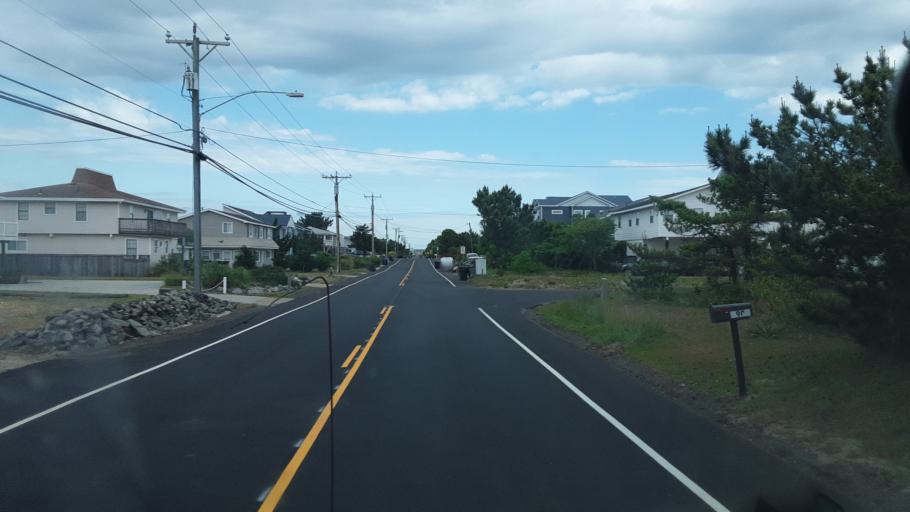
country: US
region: Virginia
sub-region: City of Virginia Beach
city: Virginia Beach
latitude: 36.7288
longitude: -75.9387
